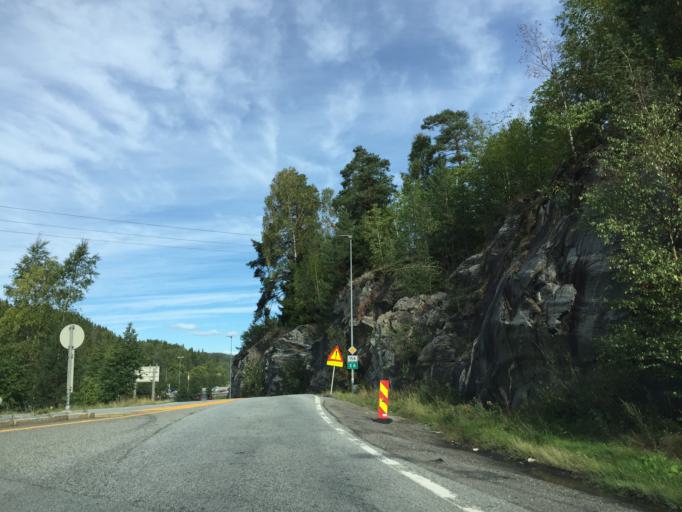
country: NO
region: Akershus
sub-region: As
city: As
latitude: 59.7069
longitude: 10.7397
